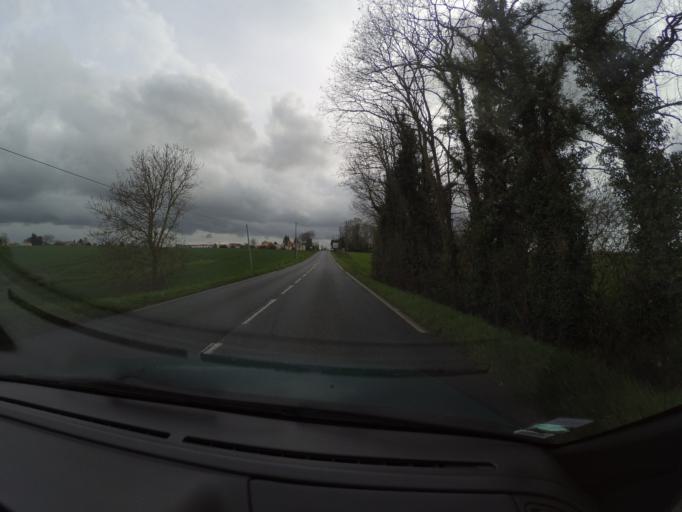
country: FR
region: Pays de la Loire
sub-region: Departement de la Loire-Atlantique
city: La Remaudiere
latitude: 47.2420
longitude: -1.2129
